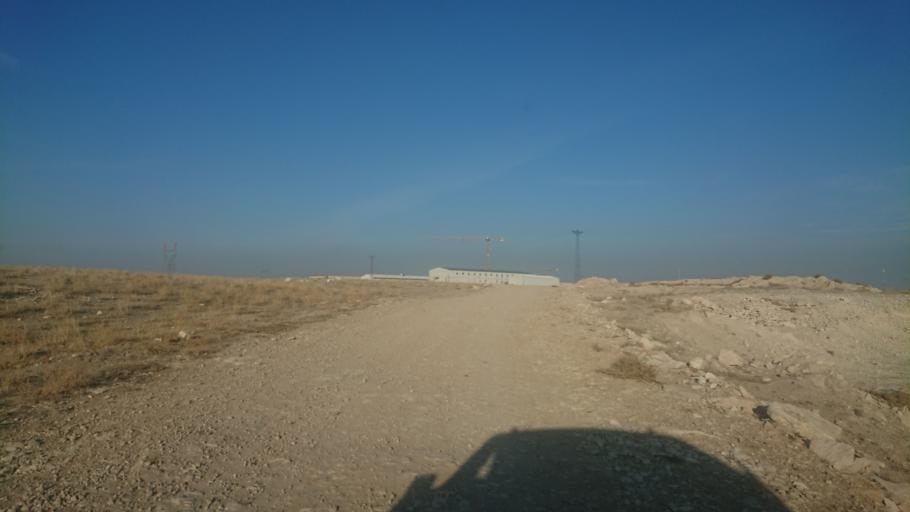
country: TR
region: Aksaray
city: Sultanhani
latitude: 38.1458
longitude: 33.5859
